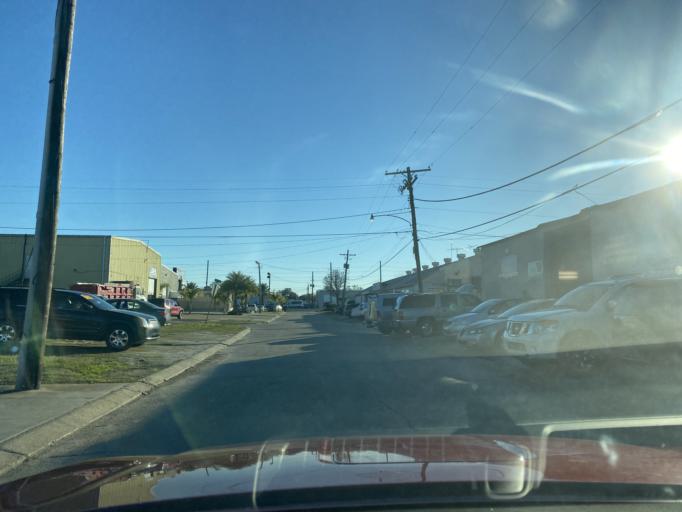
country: US
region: Louisiana
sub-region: Jefferson Parish
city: Kenner
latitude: 29.9820
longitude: -90.2489
